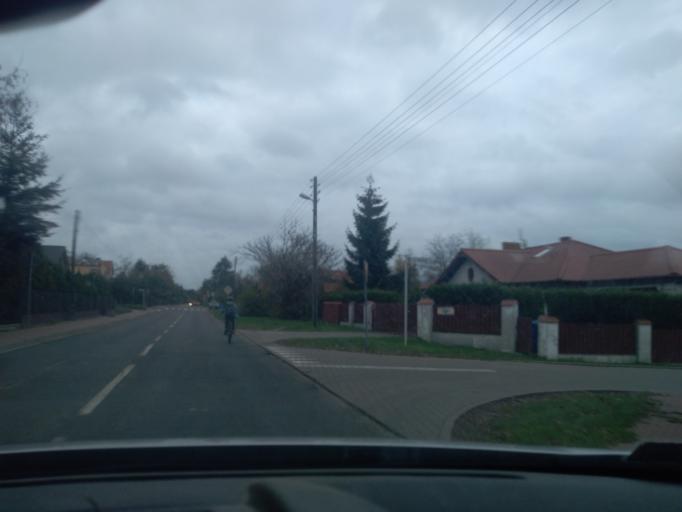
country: PL
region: Greater Poland Voivodeship
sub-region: Powiat poznanski
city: Suchy Las
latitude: 52.4750
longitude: 16.8855
